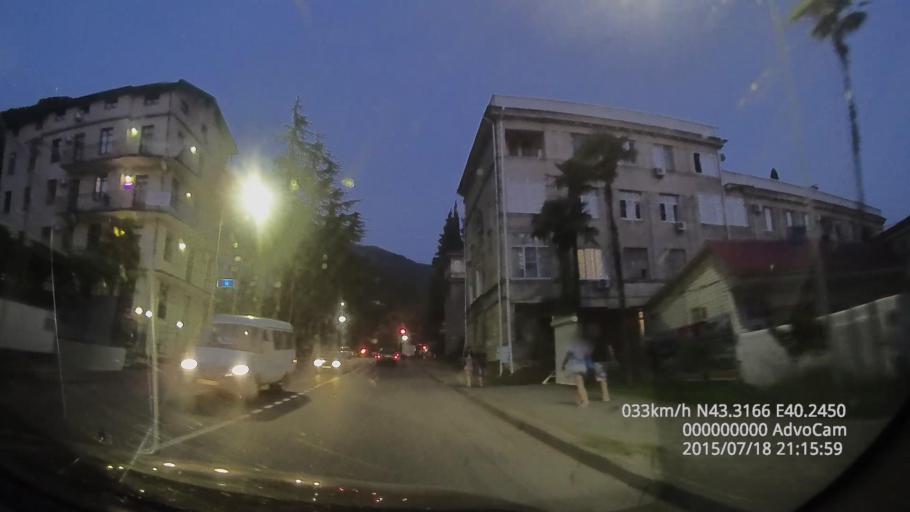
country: GE
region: Abkhazia
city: Gagra
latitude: 43.3165
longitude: 40.2454
